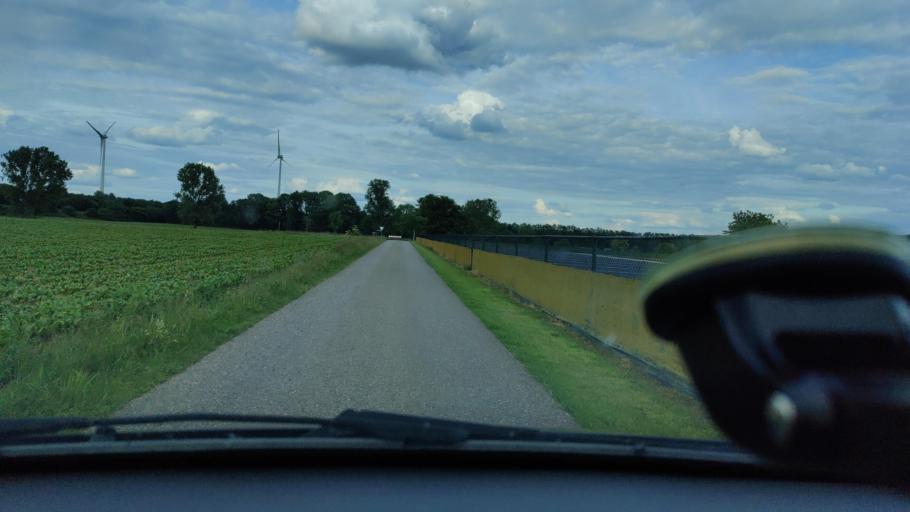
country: DE
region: North Rhine-Westphalia
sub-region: Regierungsbezirk Dusseldorf
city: Weeze
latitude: 51.6509
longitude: 6.1892
